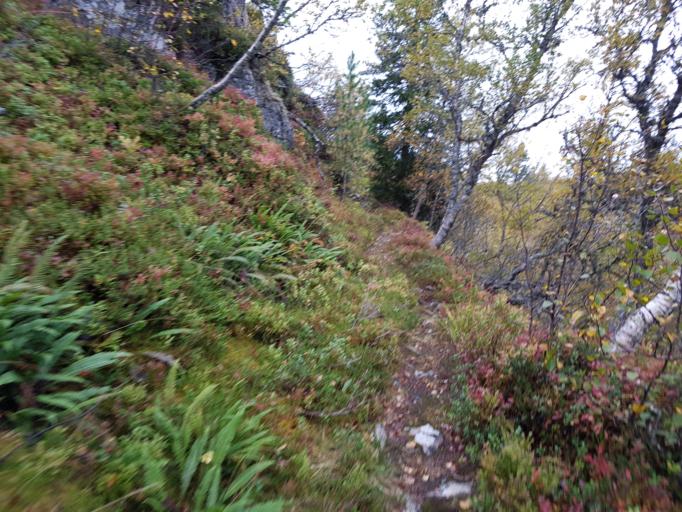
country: NO
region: Sor-Trondelag
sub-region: Melhus
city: Melhus
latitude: 63.4171
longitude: 10.2140
